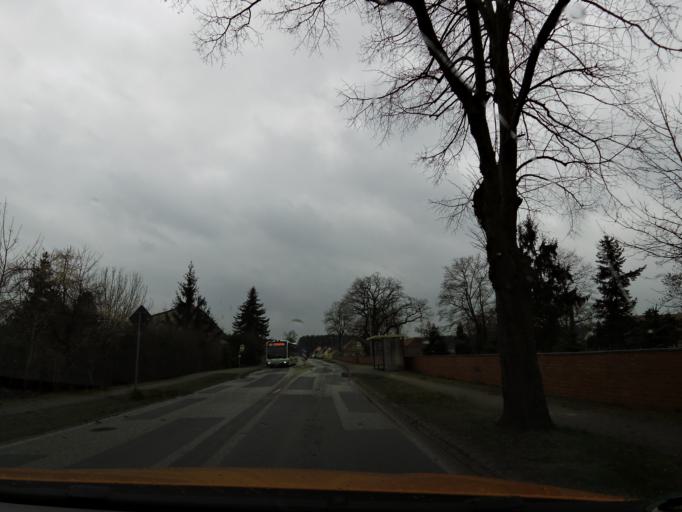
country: DE
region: Brandenburg
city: Ziesar
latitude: 52.2826
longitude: 12.3276
